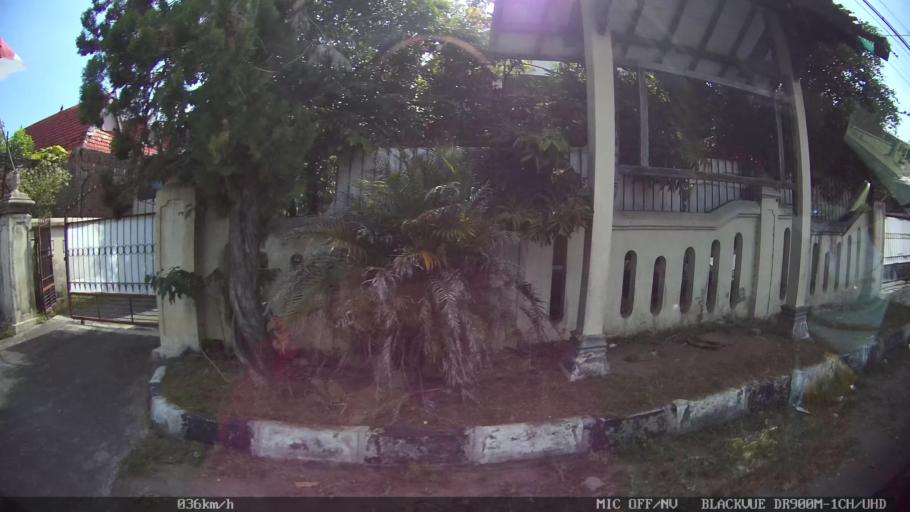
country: ID
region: Daerah Istimewa Yogyakarta
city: Yogyakarta
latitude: -7.8242
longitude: 110.3953
